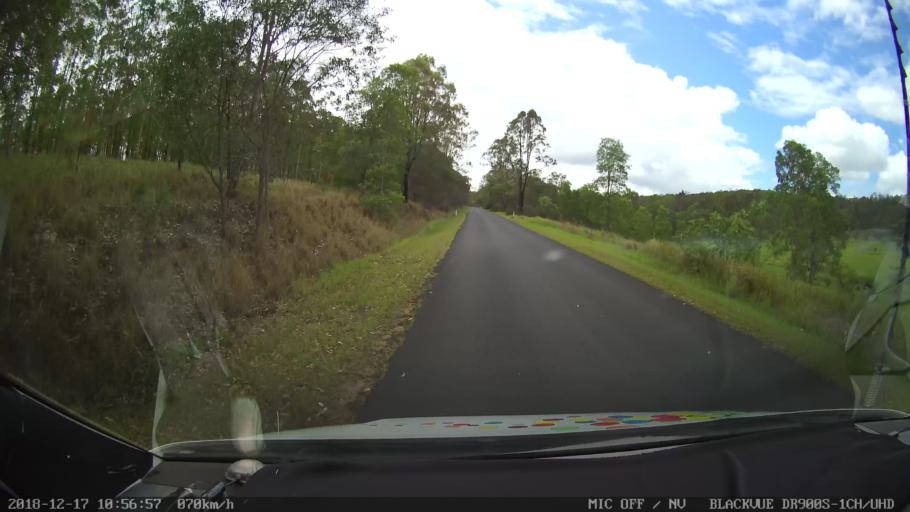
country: AU
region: New South Wales
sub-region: Richmond Valley
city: Casino
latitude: -28.8229
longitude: 152.5925
